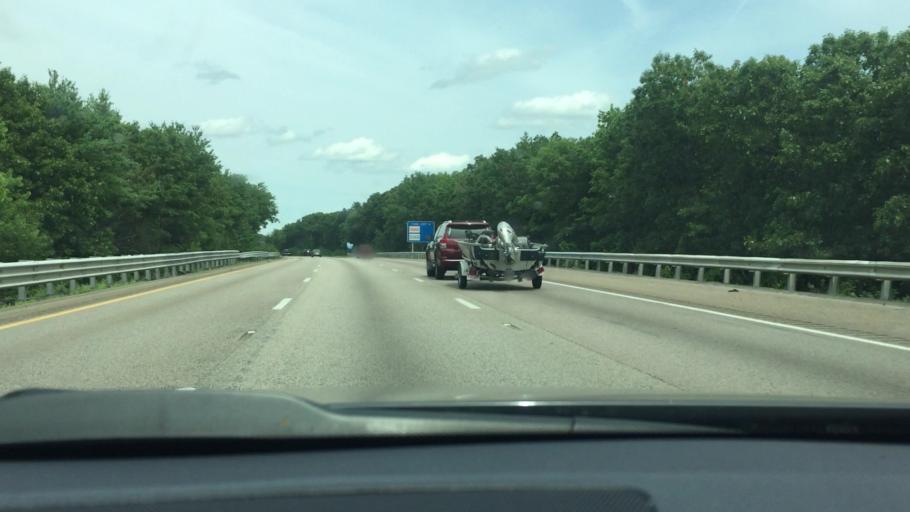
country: US
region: Massachusetts
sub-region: Norfolk County
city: Foxborough
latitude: 42.0769
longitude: -71.2231
